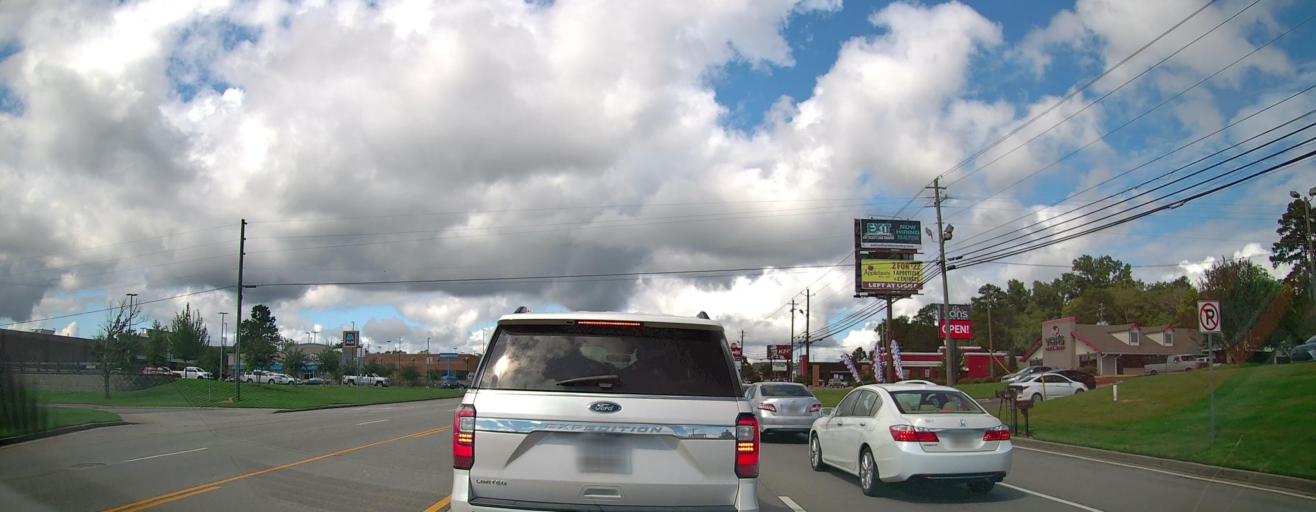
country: US
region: Georgia
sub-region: Baldwin County
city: Milledgeville
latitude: 33.1072
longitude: -83.2531
